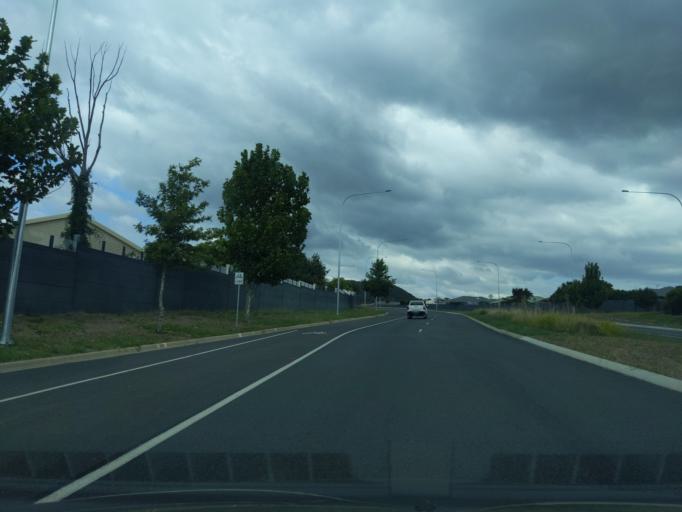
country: AU
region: New South Wales
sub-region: Queanbeyan
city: Queanbeyan
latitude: -35.3510
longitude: 149.2472
